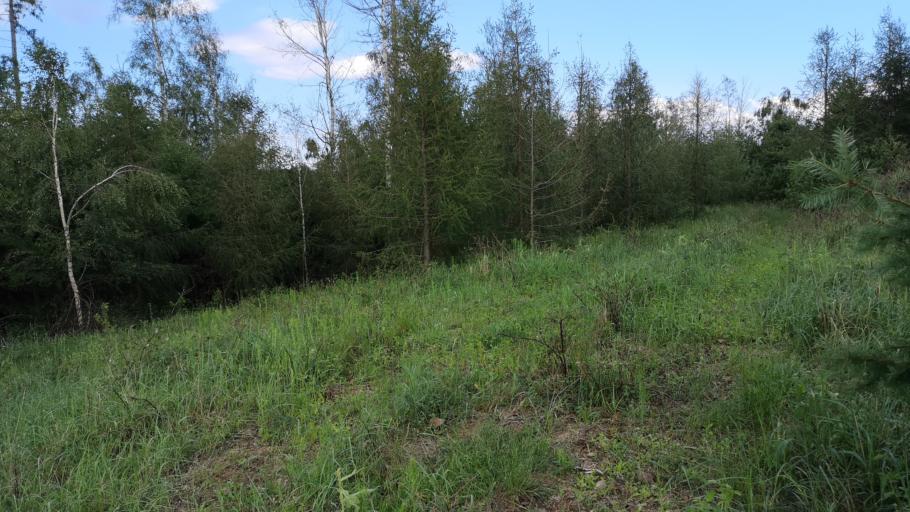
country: DE
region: Saxony-Anhalt
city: Ballenstedt
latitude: 51.6878
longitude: 11.2198
